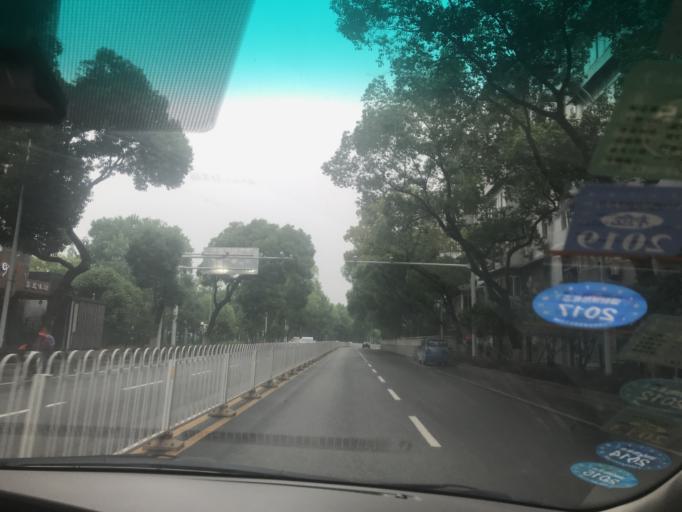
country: CN
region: Hubei
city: Wuhan
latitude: 30.5524
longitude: 114.2703
